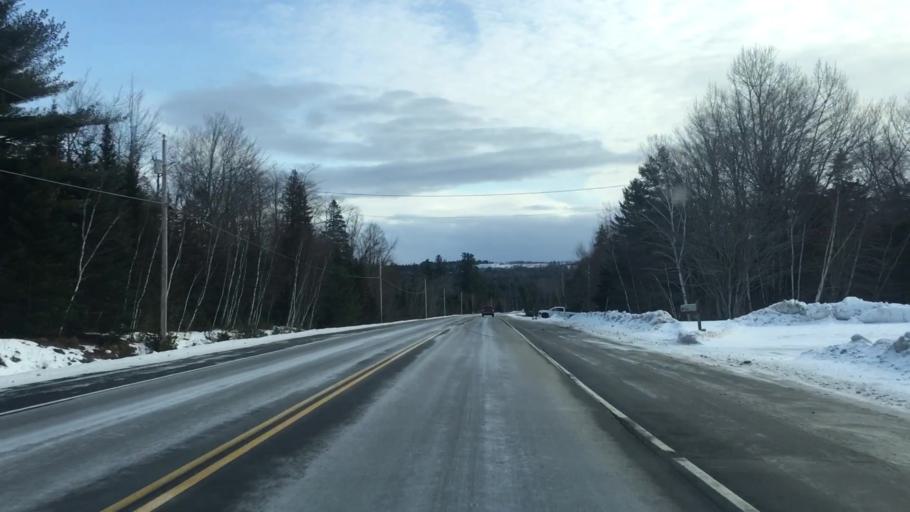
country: US
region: Maine
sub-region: Washington County
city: Machias
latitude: 44.9492
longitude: -67.6914
